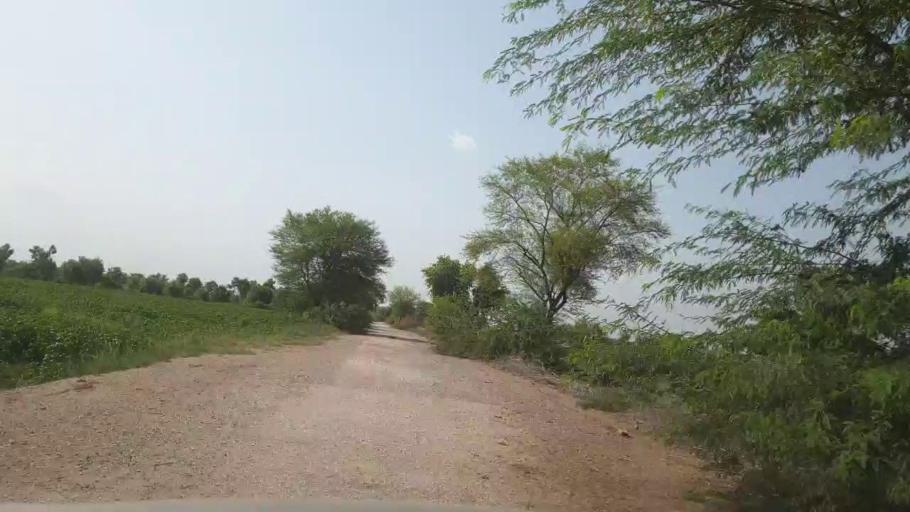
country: PK
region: Sindh
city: Pano Aqil
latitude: 27.7751
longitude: 69.1629
